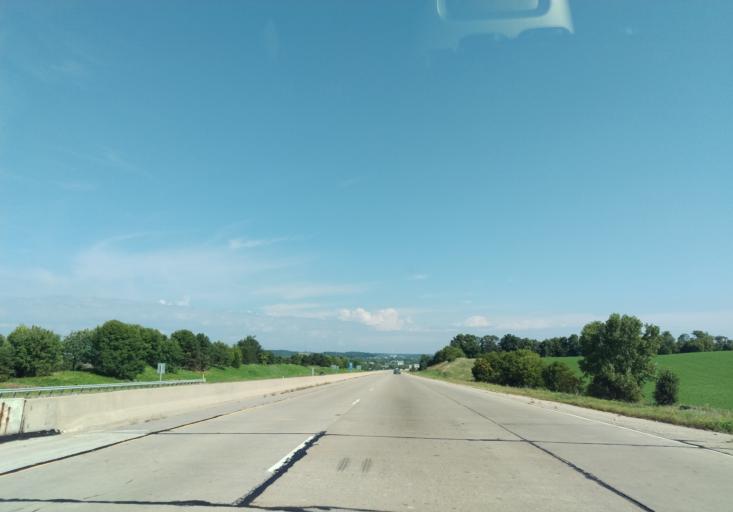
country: US
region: Wisconsin
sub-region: Dane County
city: Verona
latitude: 42.9796
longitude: -89.5120
